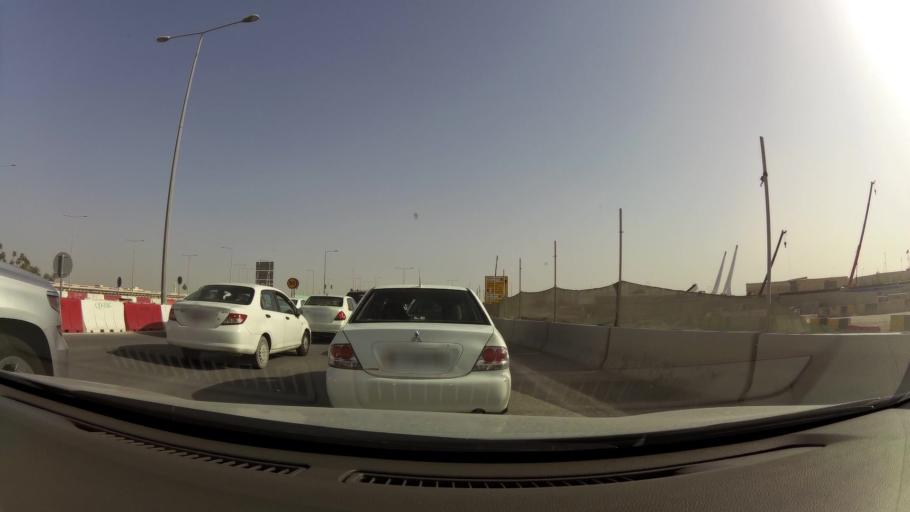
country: QA
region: Baladiyat ar Rayyan
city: Ar Rayyan
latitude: 25.3225
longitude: 51.4485
